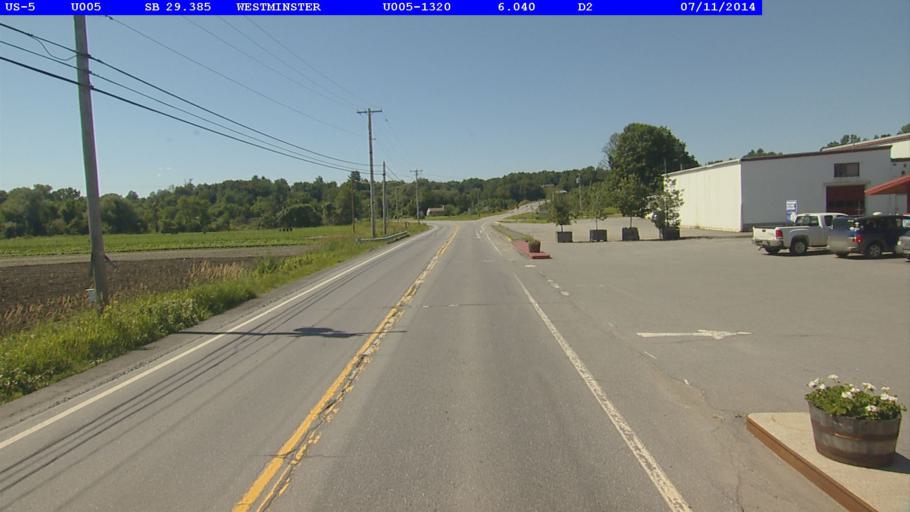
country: US
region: Vermont
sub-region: Windham County
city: Bellows Falls
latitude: 43.0966
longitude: -72.4437
